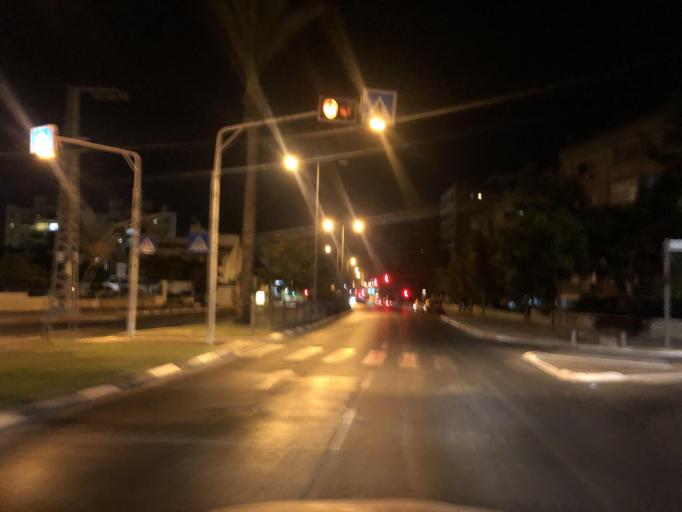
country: IL
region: Tel Aviv
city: Azor
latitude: 32.0462
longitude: 34.8030
